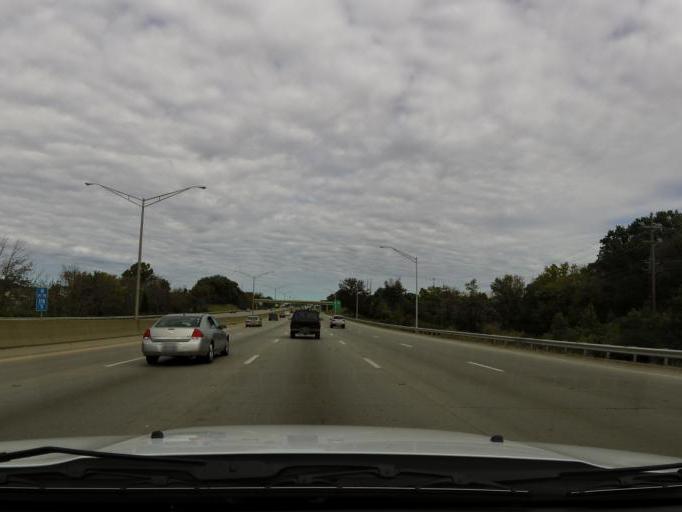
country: US
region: Kentucky
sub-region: Boone County
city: Florence
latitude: 38.9624
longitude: -84.6353
